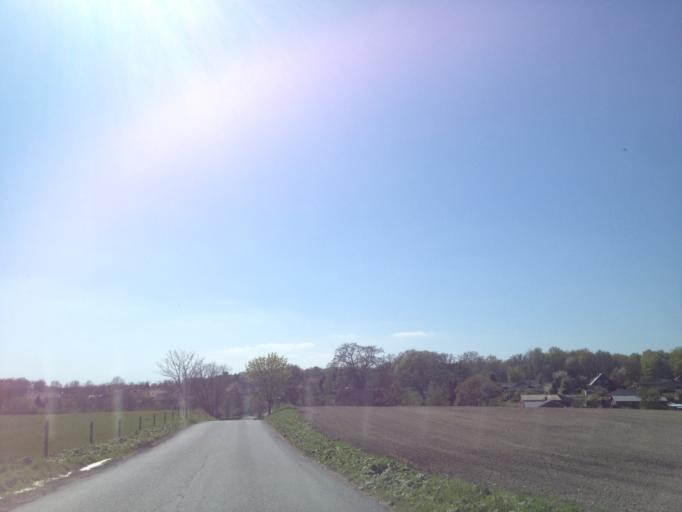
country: DK
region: Zealand
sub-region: Koge Kommune
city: Borup
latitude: 55.5085
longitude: 11.9866
